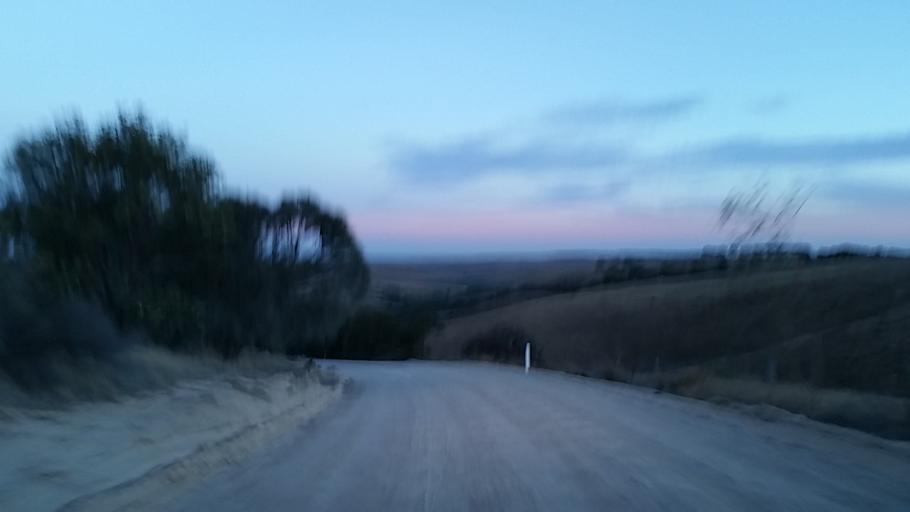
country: AU
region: South Australia
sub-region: Mount Barker
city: Callington
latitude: -35.0956
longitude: 138.9800
